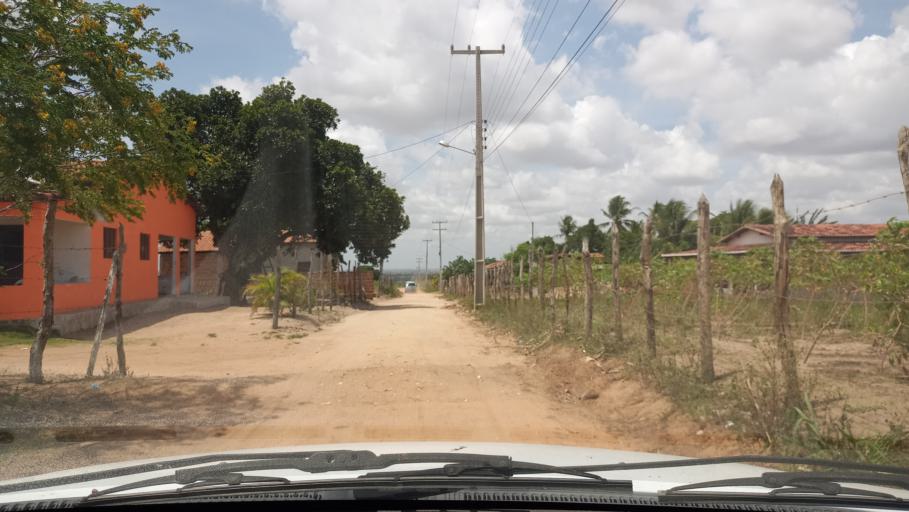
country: BR
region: Rio Grande do Norte
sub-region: Brejinho
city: Brejinho
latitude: -6.2618
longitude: -35.3414
